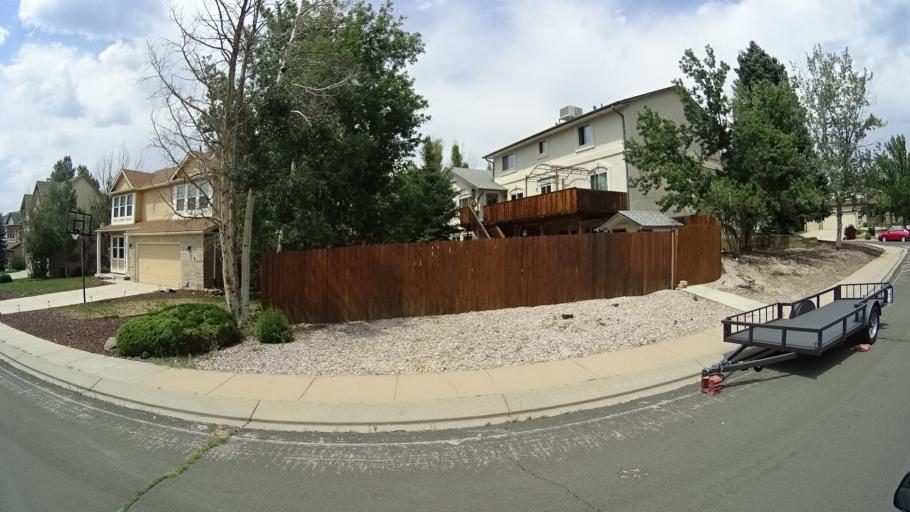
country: US
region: Colorado
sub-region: El Paso County
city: Black Forest
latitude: 38.9572
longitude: -104.7421
